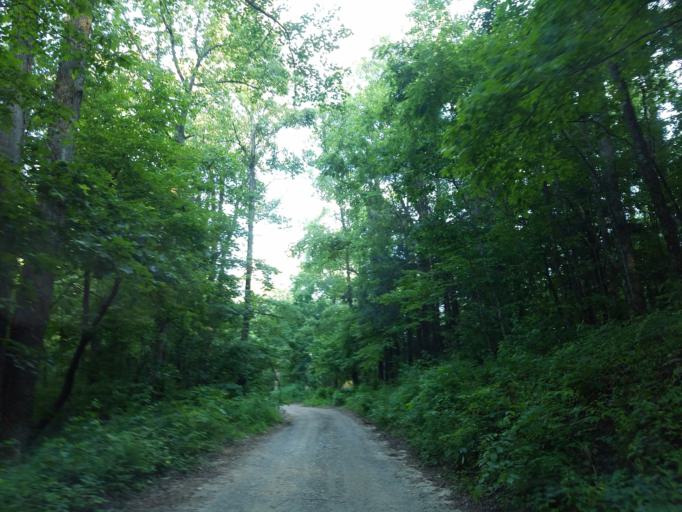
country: US
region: Georgia
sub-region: Lumpkin County
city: Dahlonega
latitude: 34.6534
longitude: -84.0856
